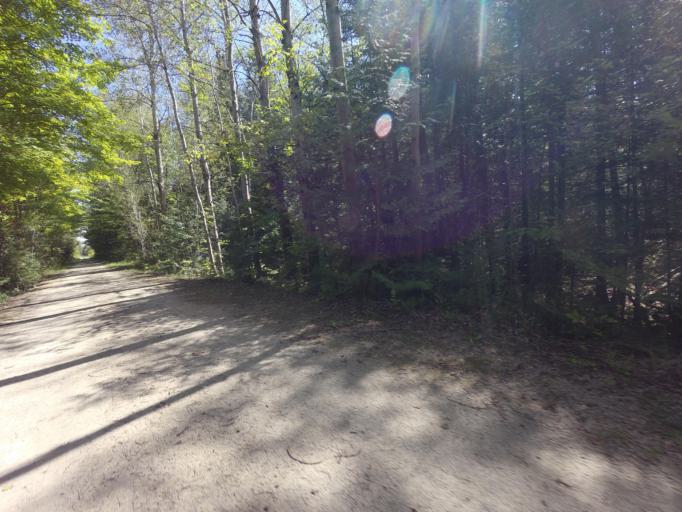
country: CA
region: Ontario
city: Orangeville
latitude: 43.7777
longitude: -80.1174
